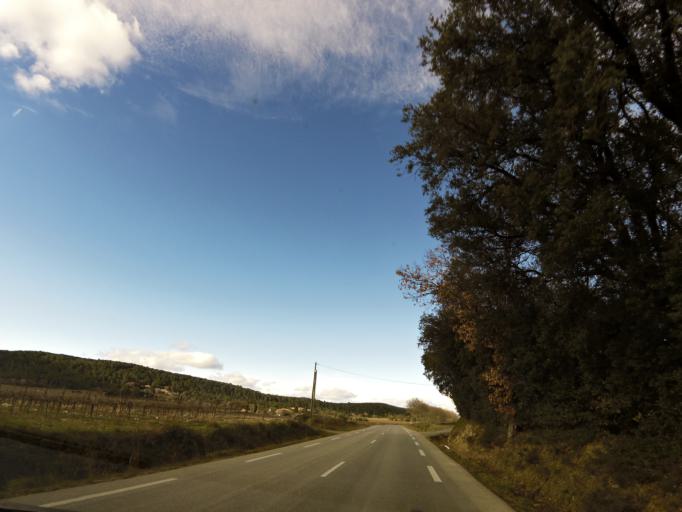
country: FR
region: Languedoc-Roussillon
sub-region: Departement du Gard
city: Quissac
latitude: 43.8509
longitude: 4.0183
